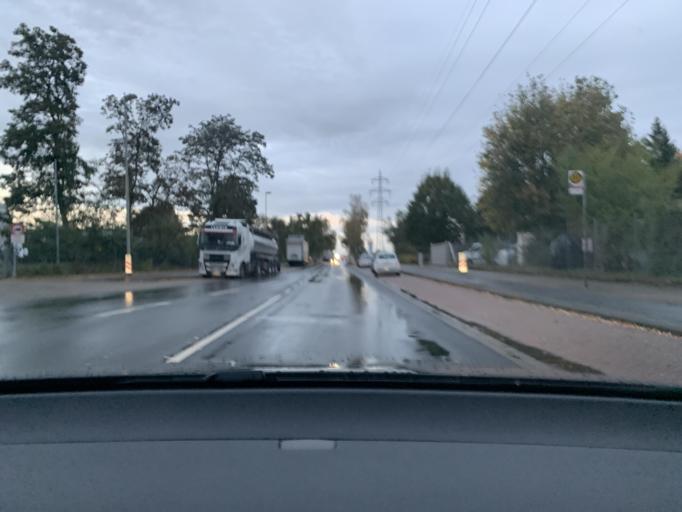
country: DE
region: Lower Saxony
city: Vordorf
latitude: 52.3144
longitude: 10.4977
